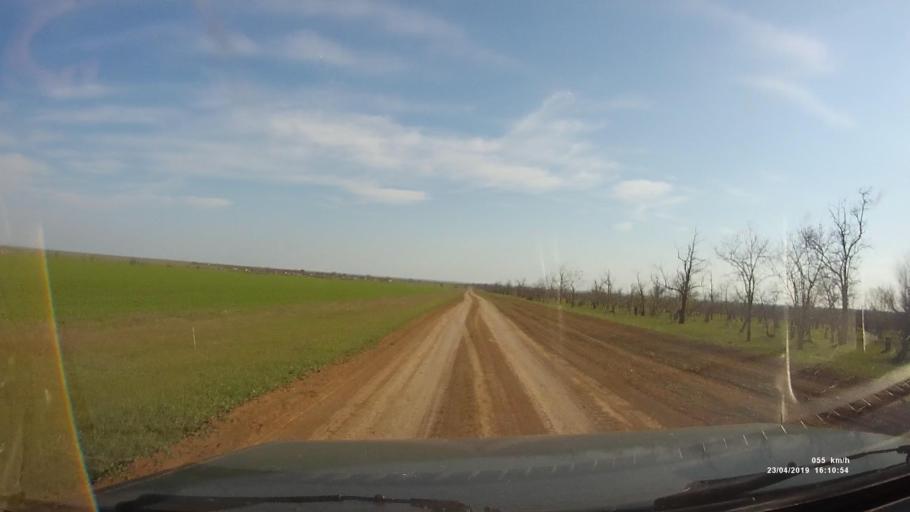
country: RU
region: Rostov
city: Remontnoye
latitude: 46.4785
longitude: 43.1231
